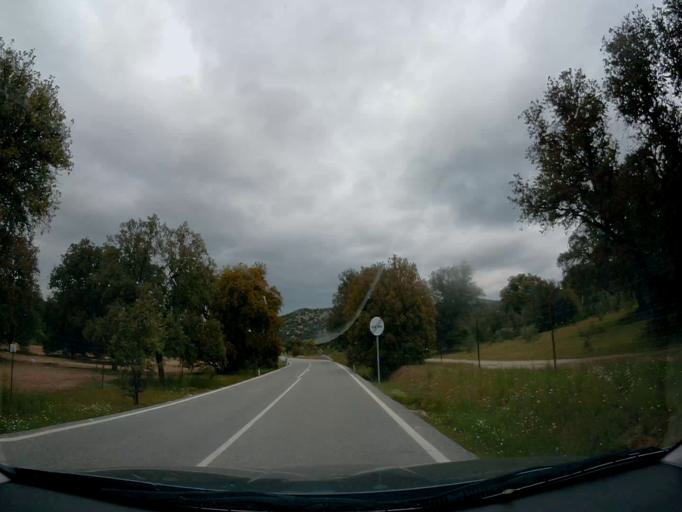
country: ES
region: Madrid
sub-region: Provincia de Madrid
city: Quijorna
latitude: 40.4264
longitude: -4.0924
